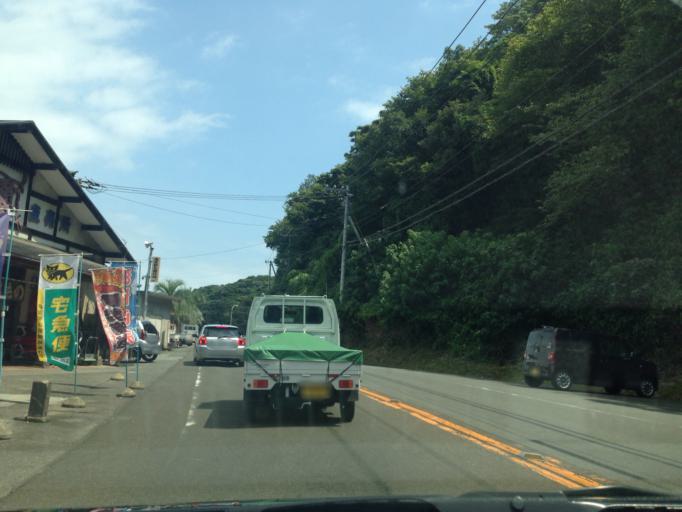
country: JP
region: Shizuoka
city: Shimoda
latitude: 34.6297
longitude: 138.8864
